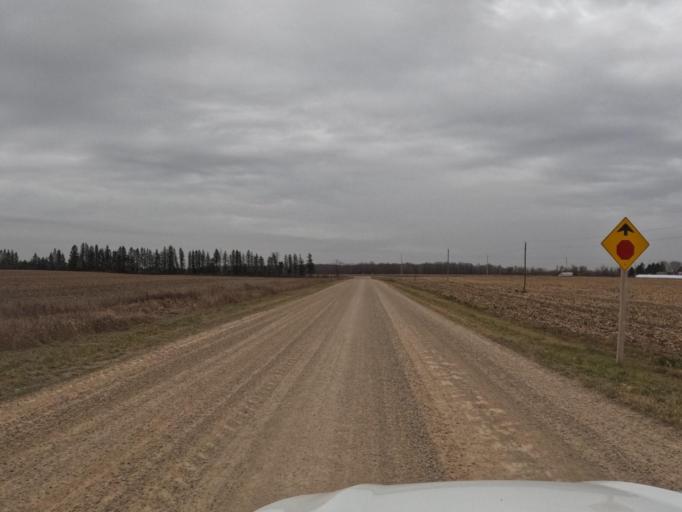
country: CA
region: Ontario
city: Shelburne
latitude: 43.8683
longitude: -80.3551
